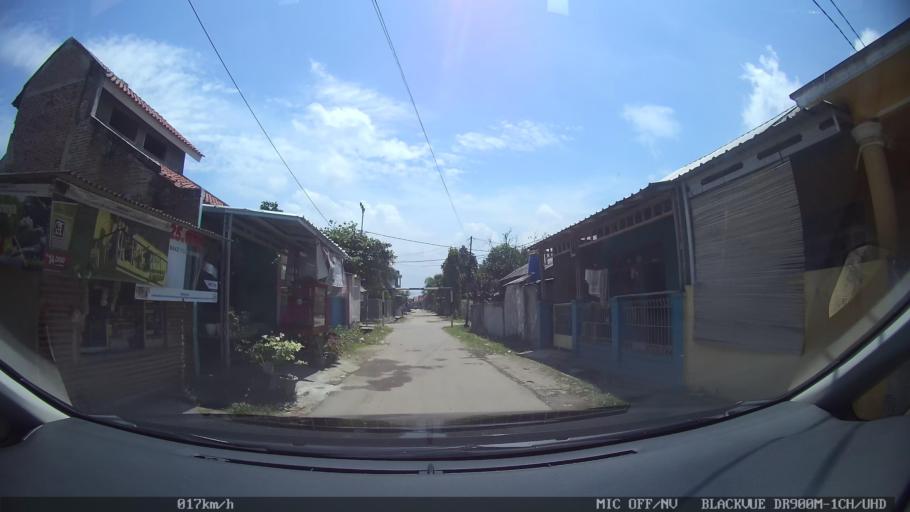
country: ID
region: Lampung
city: Kedaton
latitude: -5.3765
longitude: 105.2924
